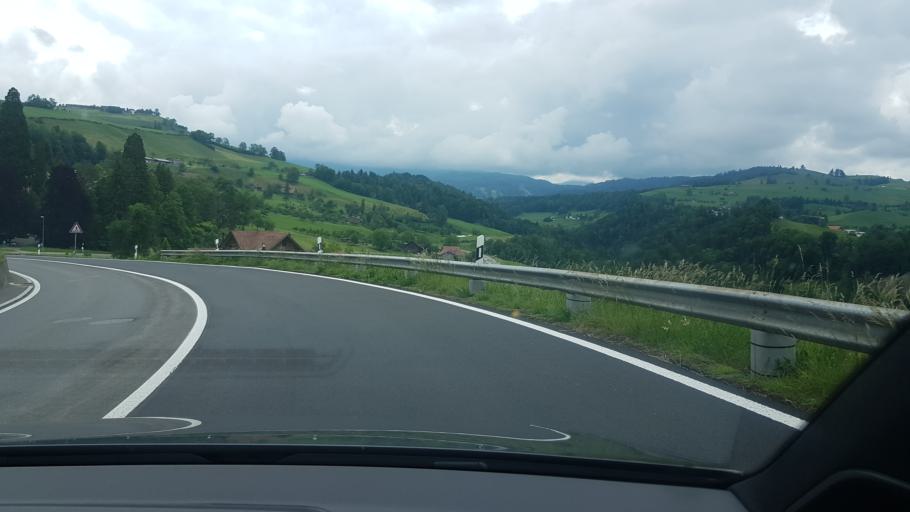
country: CH
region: Zug
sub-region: Zug
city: Menzingen
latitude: 47.1785
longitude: 8.5633
